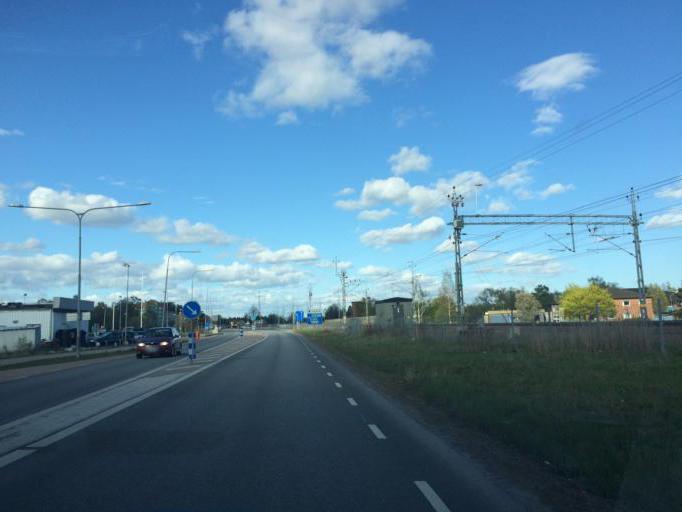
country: SE
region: Vaestmanland
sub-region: Hallstahammars Kommun
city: Kolback
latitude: 59.5607
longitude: 16.2246
